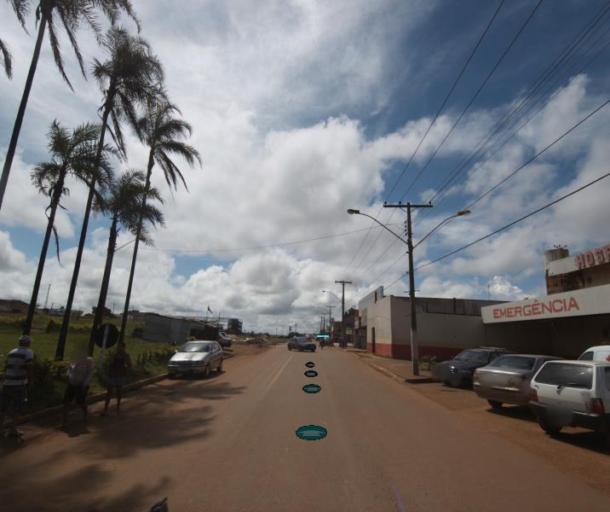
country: BR
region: Federal District
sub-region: Brasilia
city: Brasilia
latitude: -15.7378
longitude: -48.2906
